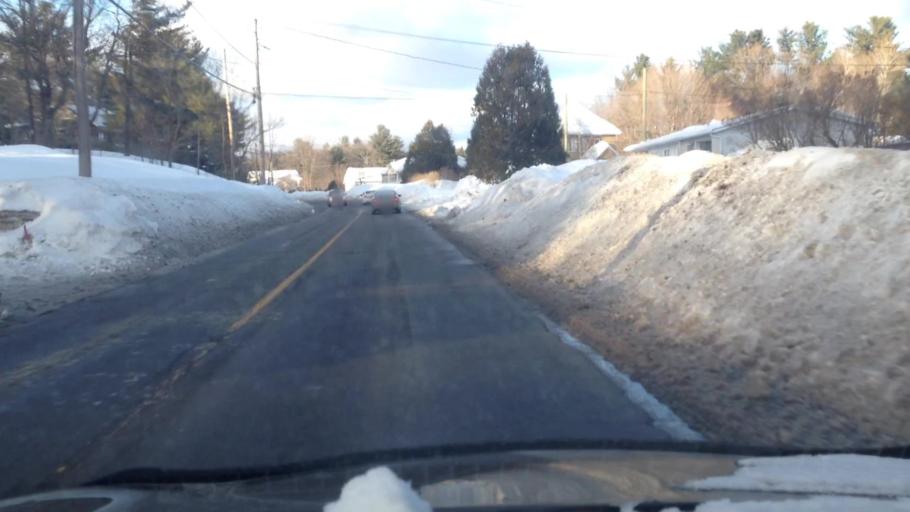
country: CA
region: Quebec
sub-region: Laurentides
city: Saint-Jerome
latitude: 45.8107
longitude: -73.9859
